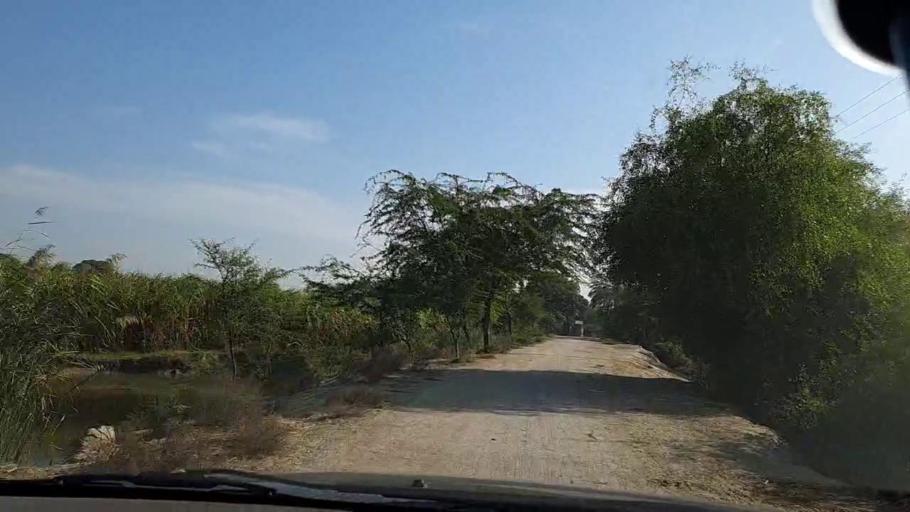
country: PK
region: Sindh
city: Mirpur Batoro
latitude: 24.6130
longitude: 68.2684
